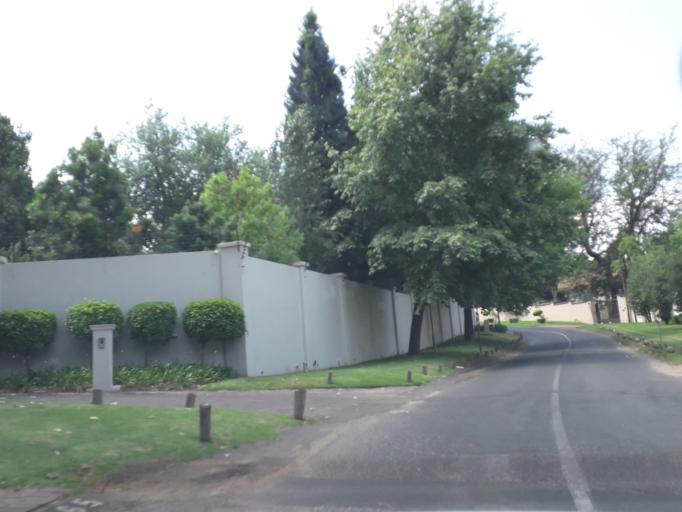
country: ZA
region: Gauteng
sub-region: City of Johannesburg Metropolitan Municipality
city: Johannesburg
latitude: -26.1198
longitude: 28.0578
